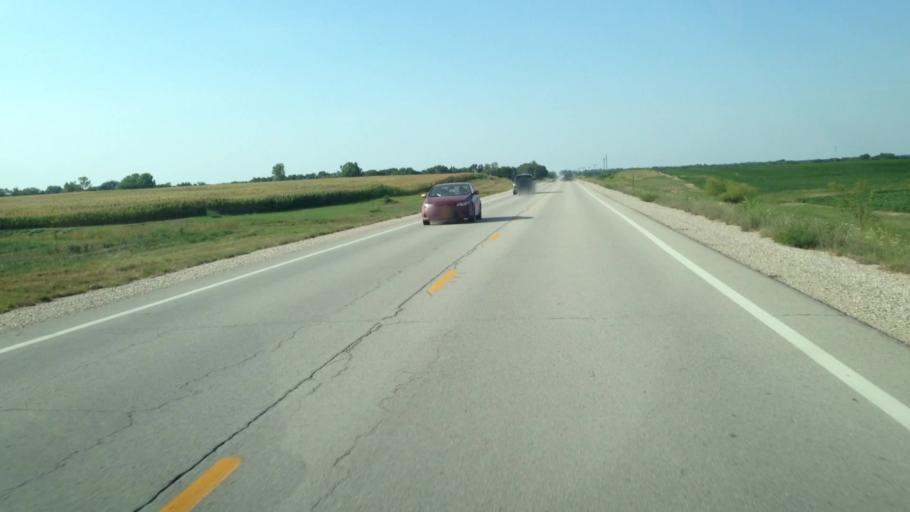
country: US
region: Kansas
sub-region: Anderson County
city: Garnett
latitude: 38.0917
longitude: -95.2431
